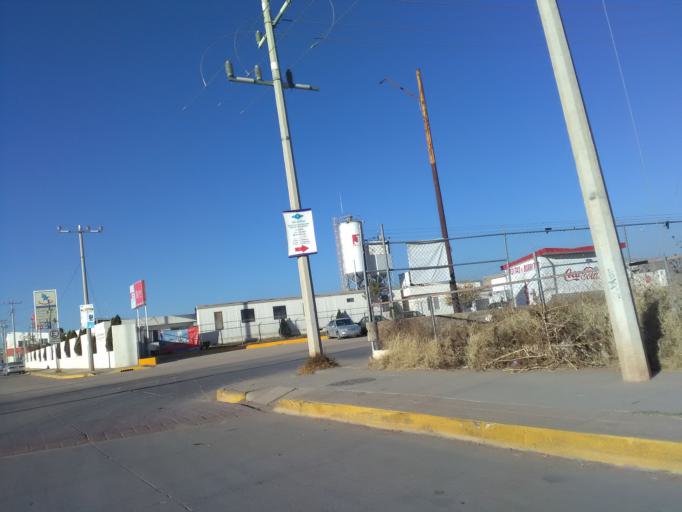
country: MX
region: Durango
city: Victoria de Durango
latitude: 24.0511
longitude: -104.6467
